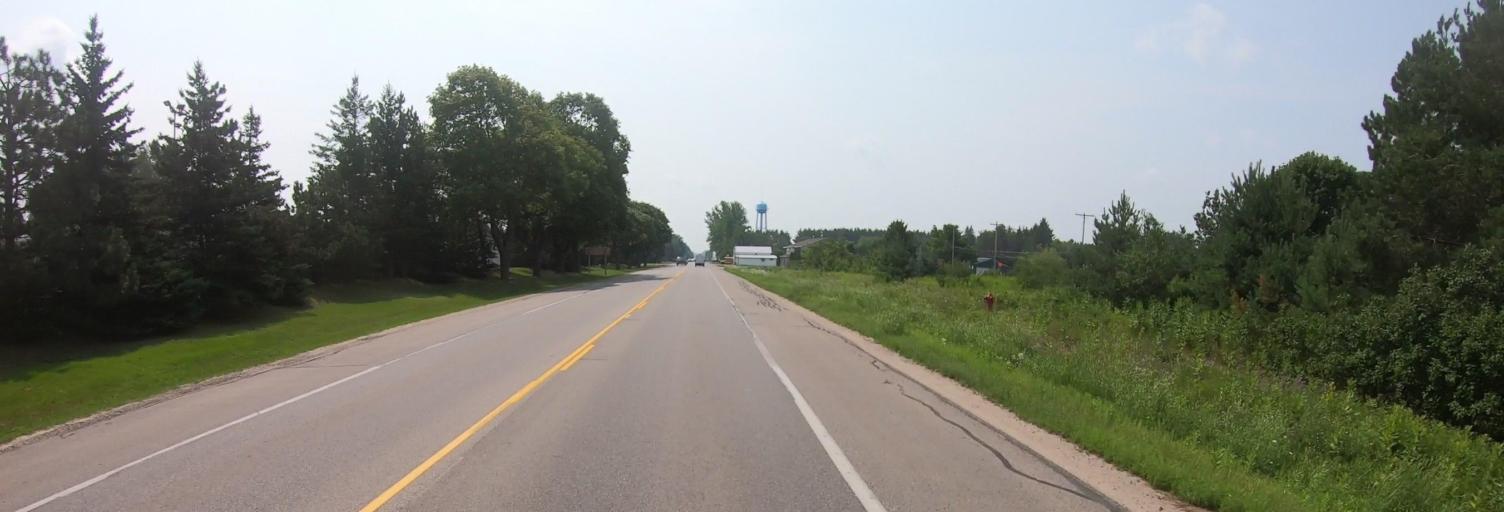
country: US
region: Michigan
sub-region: Luce County
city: Newberry
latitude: 46.3311
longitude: -85.5097
